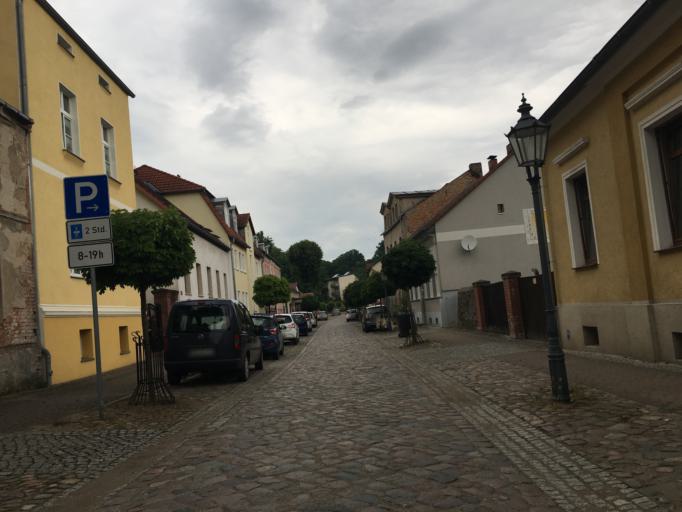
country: DE
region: Brandenburg
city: Oderberg
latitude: 52.8686
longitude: 14.0430
